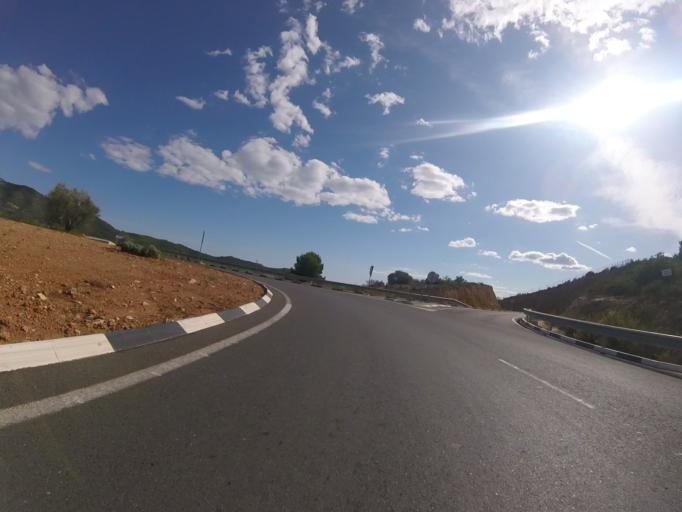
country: ES
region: Valencia
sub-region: Provincia de Castello
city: Alcala de Xivert
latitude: 40.2682
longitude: 0.2398
